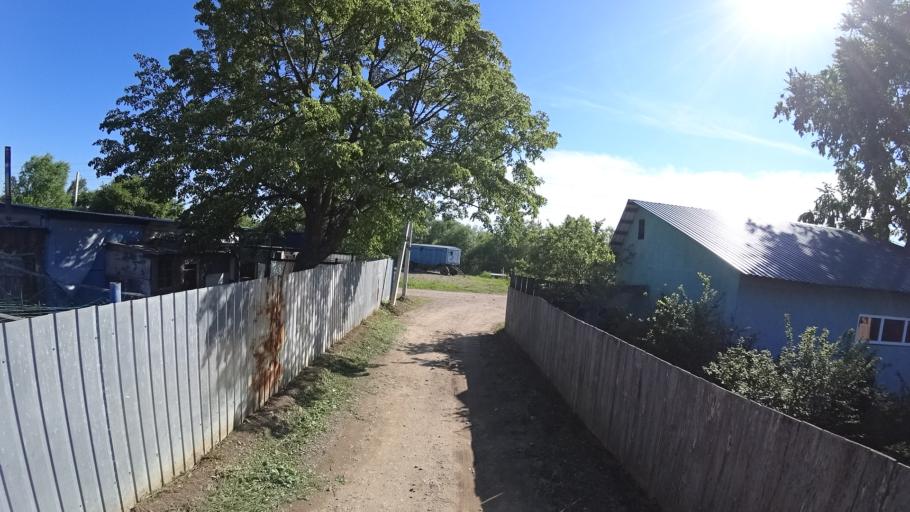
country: RU
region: Khabarovsk Krai
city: Khor
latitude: 47.8854
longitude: 135.0184
